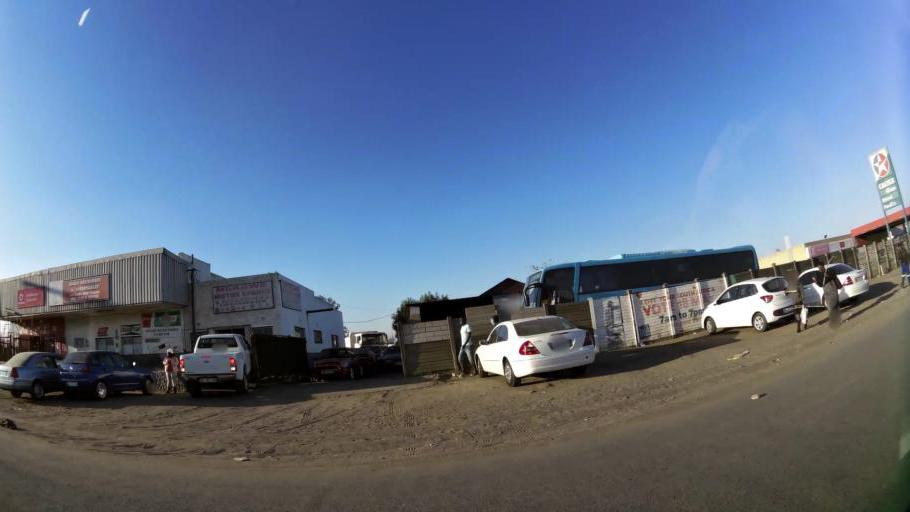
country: ZA
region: North-West
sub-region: Bojanala Platinum District Municipality
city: Rustenburg
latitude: -25.6357
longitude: 27.2200
